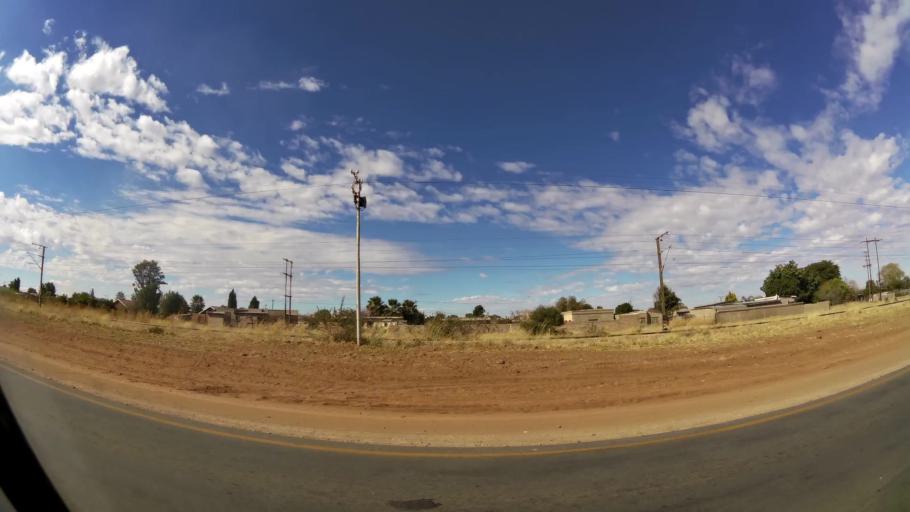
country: ZA
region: Limpopo
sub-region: Waterberg District Municipality
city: Bela-Bela
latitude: -24.8732
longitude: 28.3178
